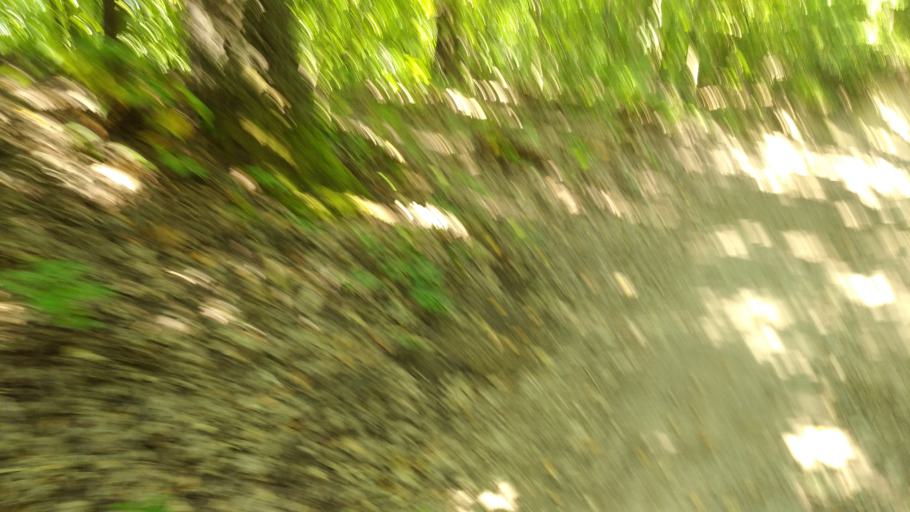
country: HU
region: Komarom-Esztergom
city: Pilismarot
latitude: 47.7848
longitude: 18.9130
